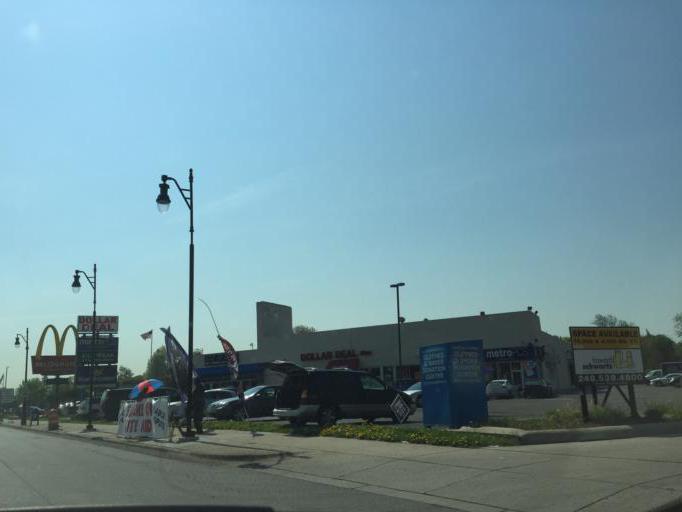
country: US
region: Michigan
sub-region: Oakland County
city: Oak Park
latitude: 42.4026
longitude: -83.2231
